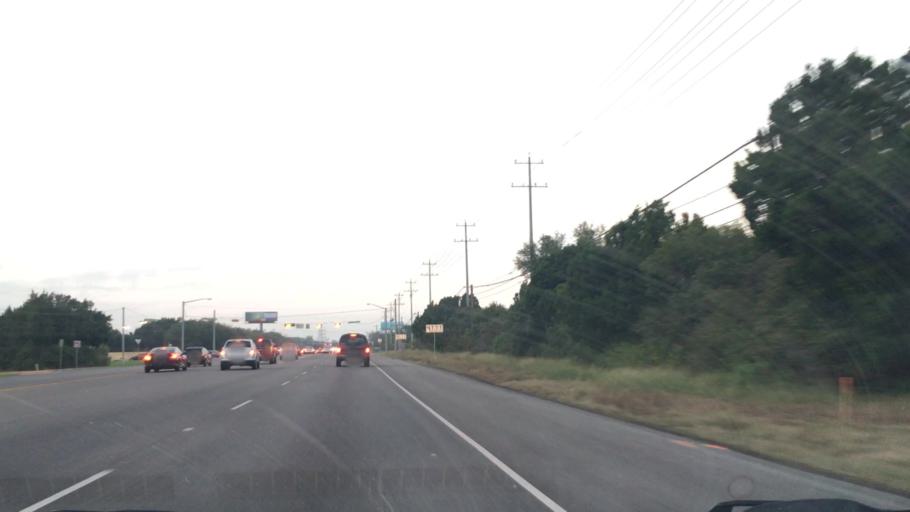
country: US
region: Texas
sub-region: Williamson County
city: Anderson Mill
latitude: 30.4080
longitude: -97.8520
